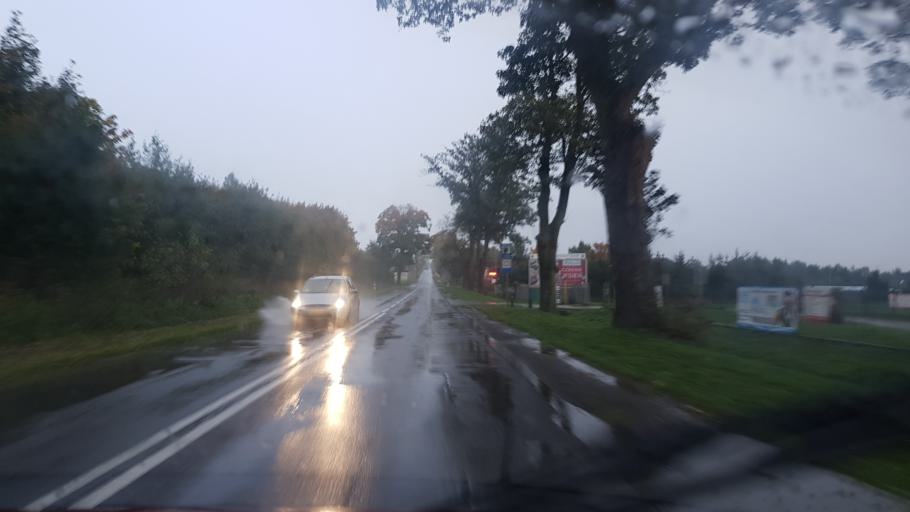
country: PL
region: Greater Poland Voivodeship
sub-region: Powiat pilski
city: Szydlowo
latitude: 53.1617
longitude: 16.6215
